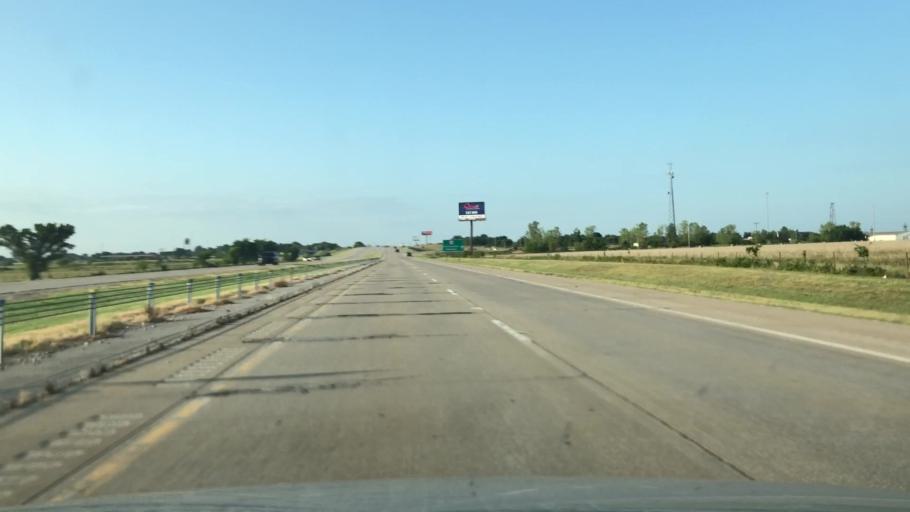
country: US
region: Oklahoma
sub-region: Osage County
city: Skiatook
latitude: 36.3725
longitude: -95.9207
